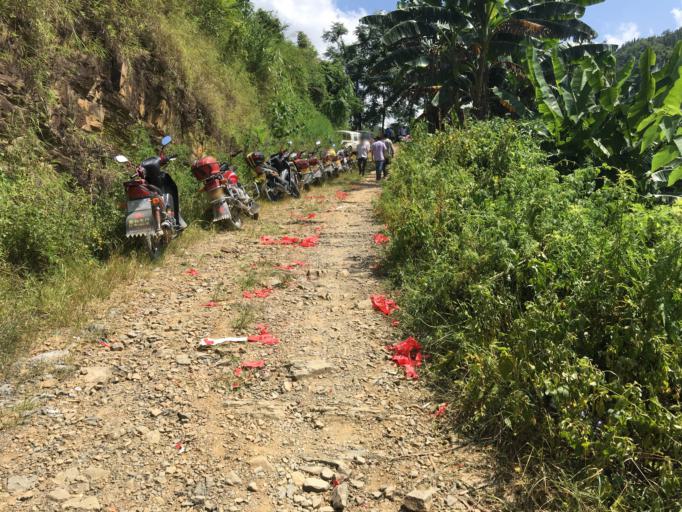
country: CN
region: Guangxi Zhuangzu Zizhiqu
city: Tongle
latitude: 24.9710
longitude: 105.9864
